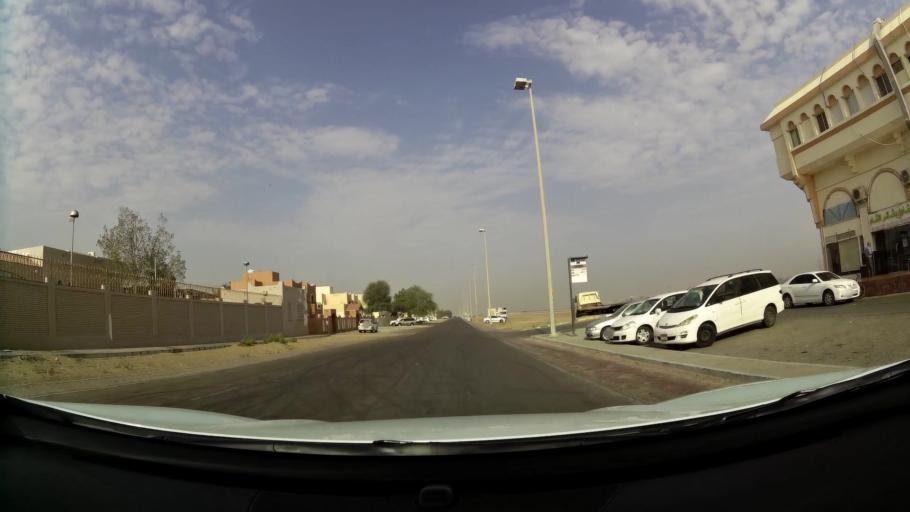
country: AE
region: Abu Dhabi
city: Abu Dhabi
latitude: 24.2421
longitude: 54.7184
